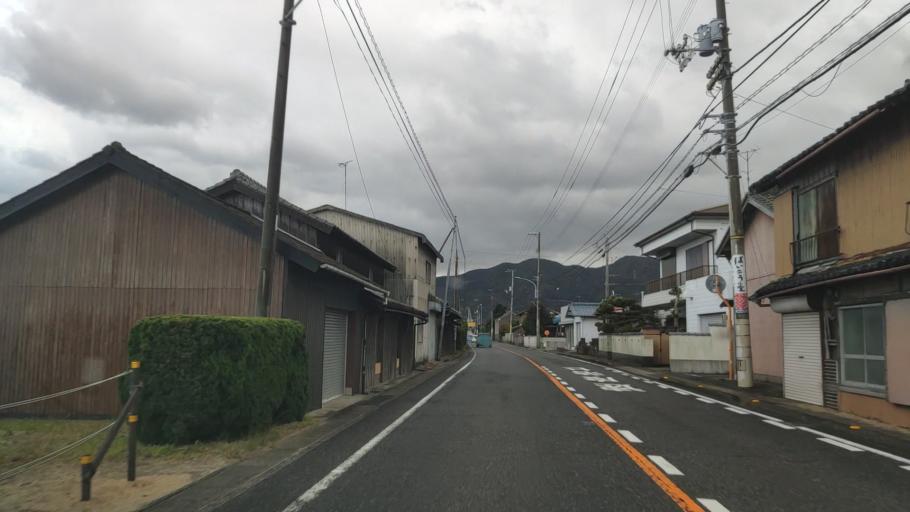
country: JP
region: Tokushima
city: Ishii
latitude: 34.2171
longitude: 134.4180
